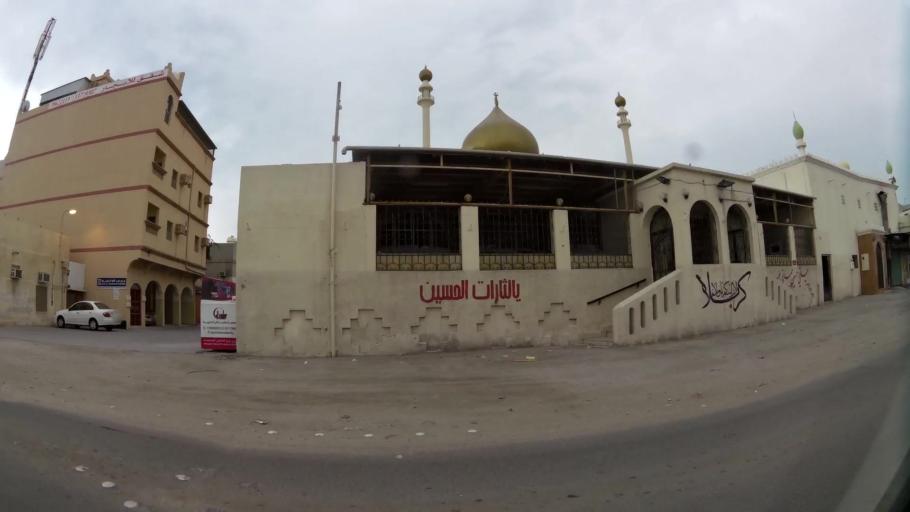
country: BH
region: Central Governorate
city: Madinat Hamad
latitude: 26.1253
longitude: 50.4769
